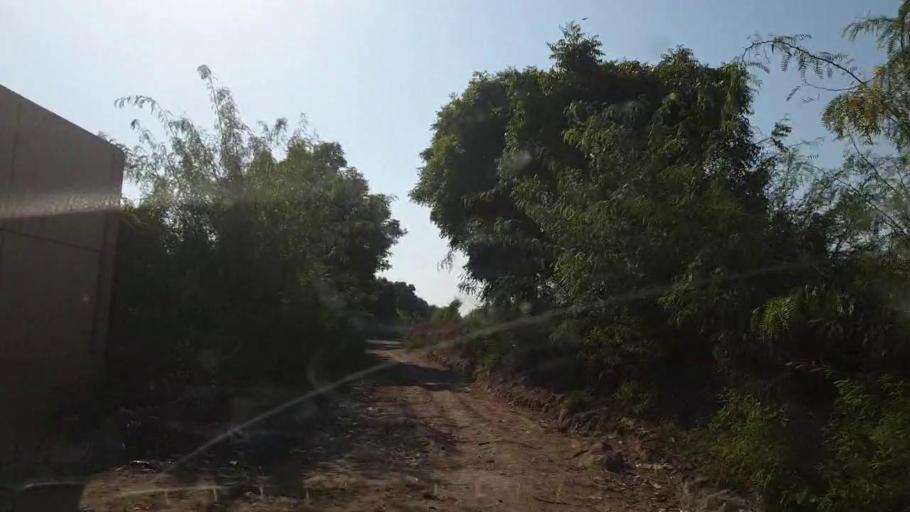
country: PK
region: Sindh
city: Tando Jam
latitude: 25.3484
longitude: 68.5773
